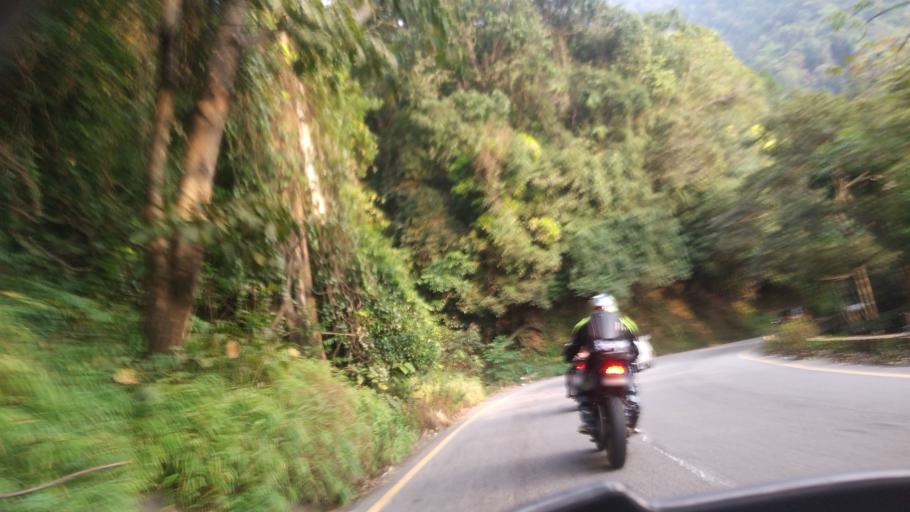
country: IN
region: Kerala
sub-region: Wayanad
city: Kalpetta
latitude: 11.5076
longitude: 76.0292
